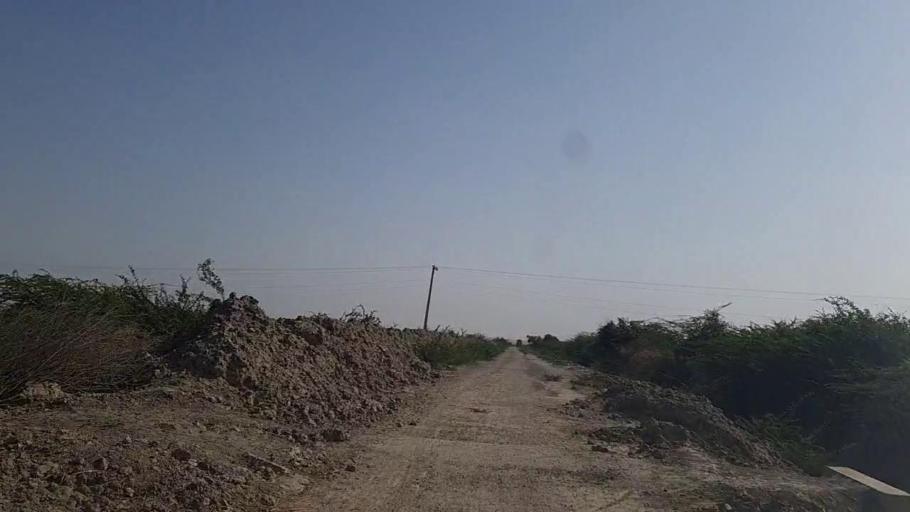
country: PK
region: Sindh
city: Kadhan
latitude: 24.5808
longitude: 69.2628
